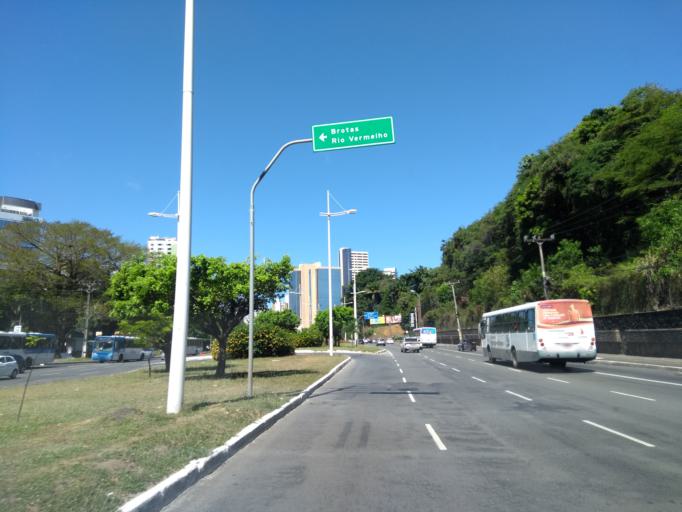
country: BR
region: Bahia
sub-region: Salvador
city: Salvador
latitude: -12.9895
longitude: -38.4722
